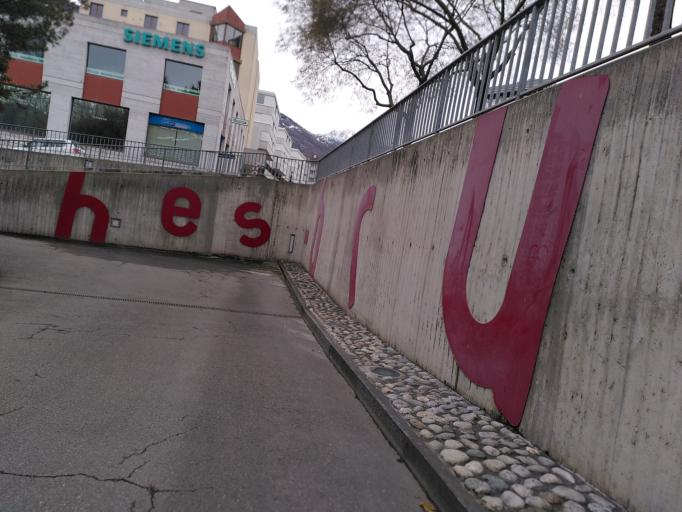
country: CH
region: Valais
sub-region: Sion District
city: Sitten
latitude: 46.2329
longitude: 7.3692
